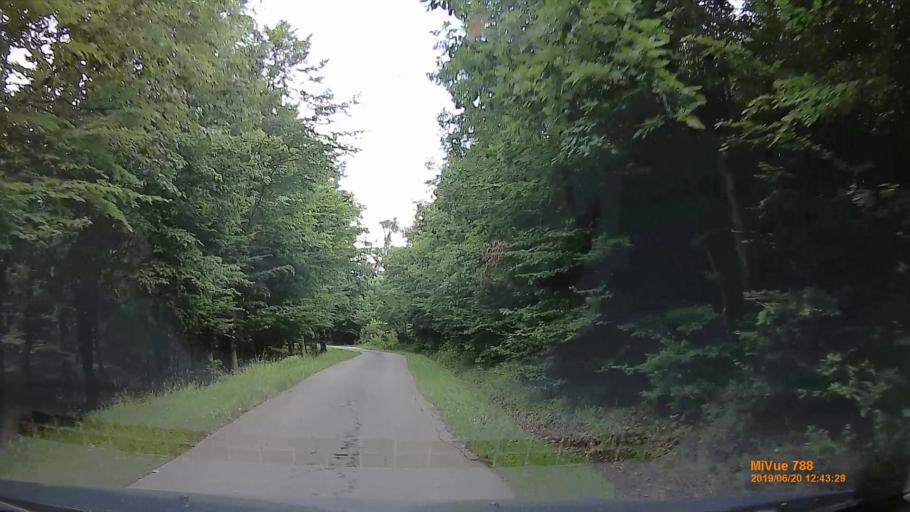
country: HU
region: Baranya
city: Hosszuheteny
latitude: 46.2012
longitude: 18.3562
